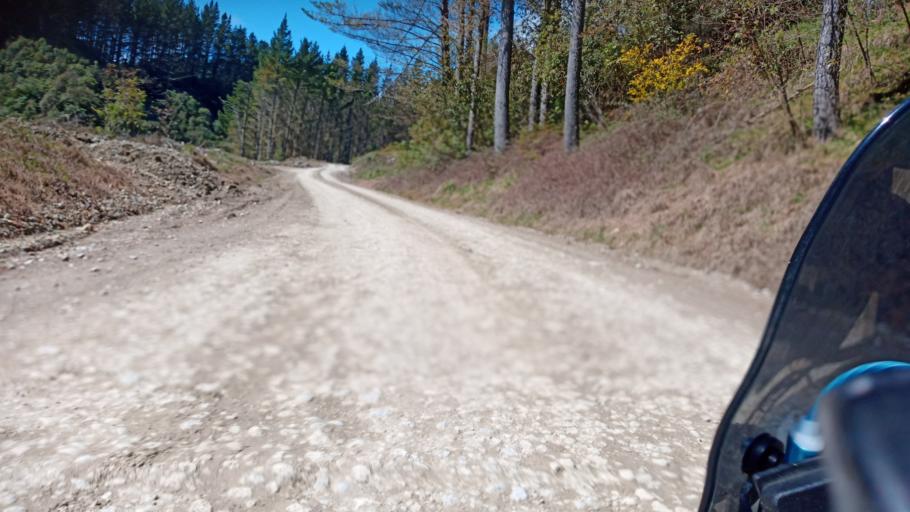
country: NZ
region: Gisborne
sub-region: Gisborne District
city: Gisborne
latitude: -38.8959
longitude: 177.8021
